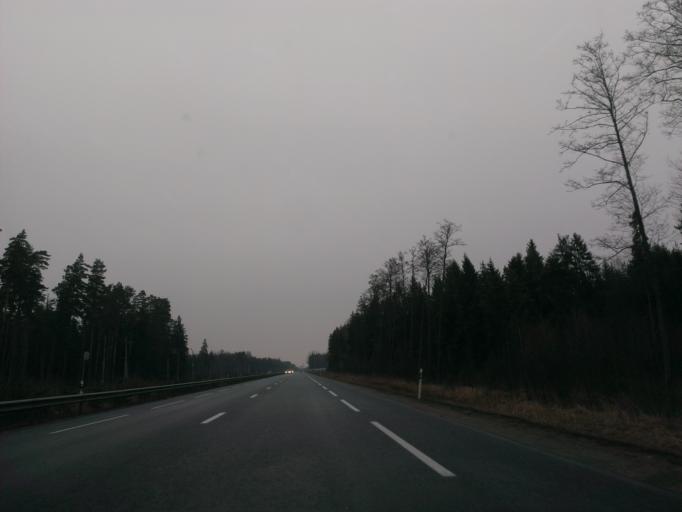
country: LV
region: Saulkrastu
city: Saulkrasti
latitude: 57.3003
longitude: 24.4402
